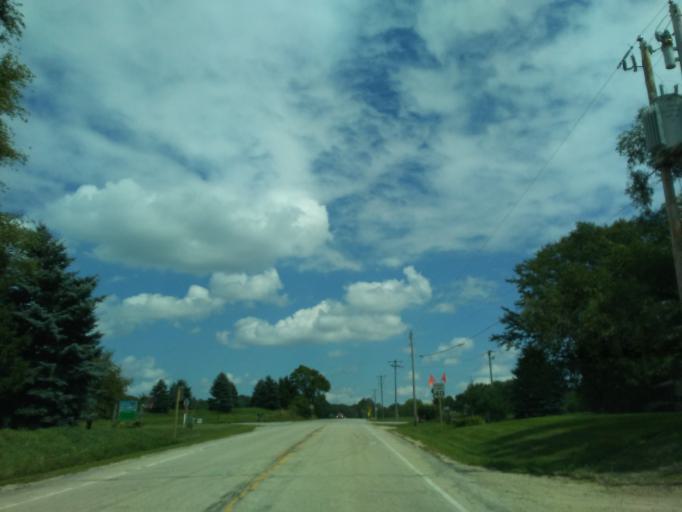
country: US
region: Wisconsin
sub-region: Dane County
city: Verona
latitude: 43.0130
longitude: -89.5640
